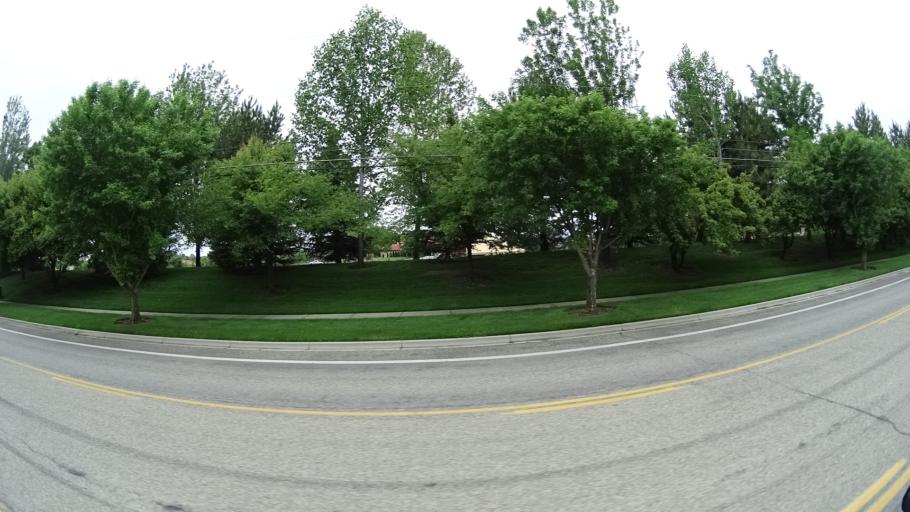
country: US
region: Idaho
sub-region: Ada County
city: Eagle
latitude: 43.7065
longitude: -116.3710
